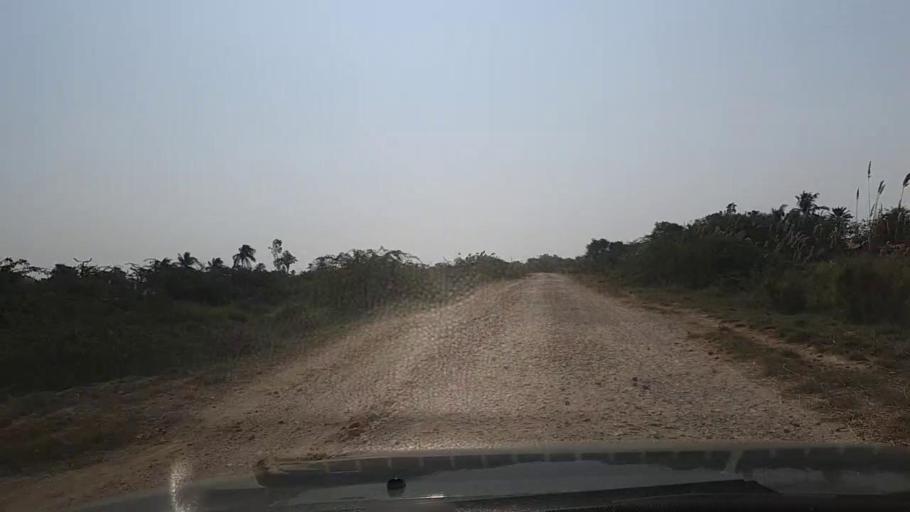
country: PK
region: Sindh
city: Mirpur Sakro
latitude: 24.4015
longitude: 67.6674
